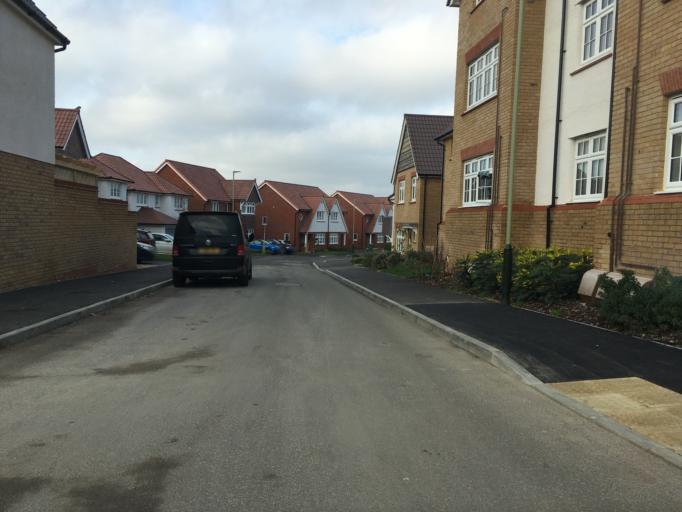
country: GB
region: England
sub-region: Gloucestershire
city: Shurdington
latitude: 51.8742
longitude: -2.0954
